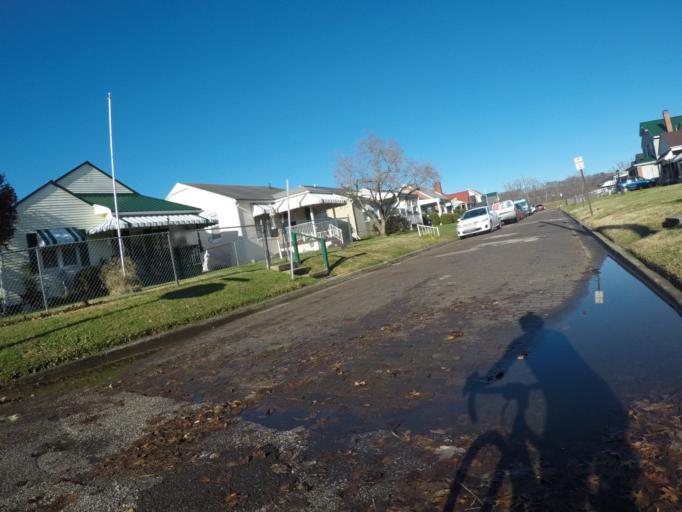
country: US
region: Ohio
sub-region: Lawrence County
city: Burlington
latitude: 38.4028
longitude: -82.5122
